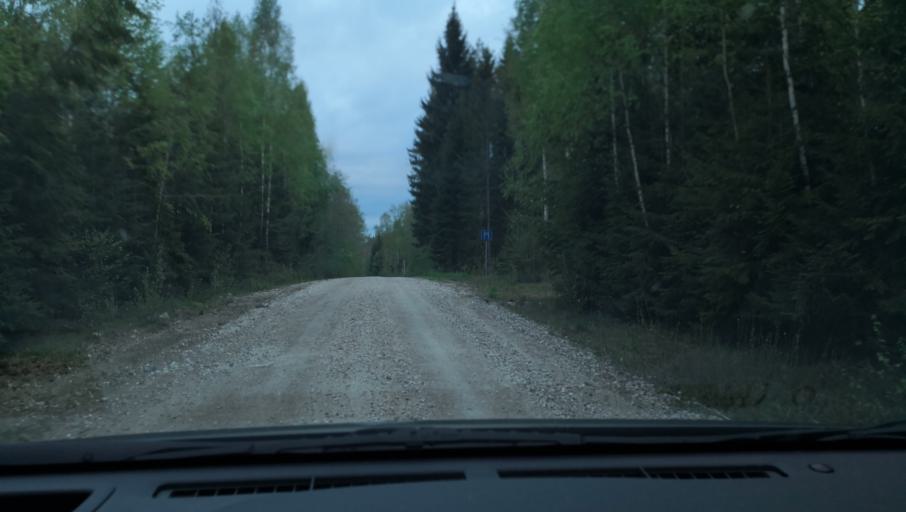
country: SE
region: Vaestmanland
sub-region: Skinnskattebergs Kommun
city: Skinnskatteberg
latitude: 59.7738
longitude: 15.4543
